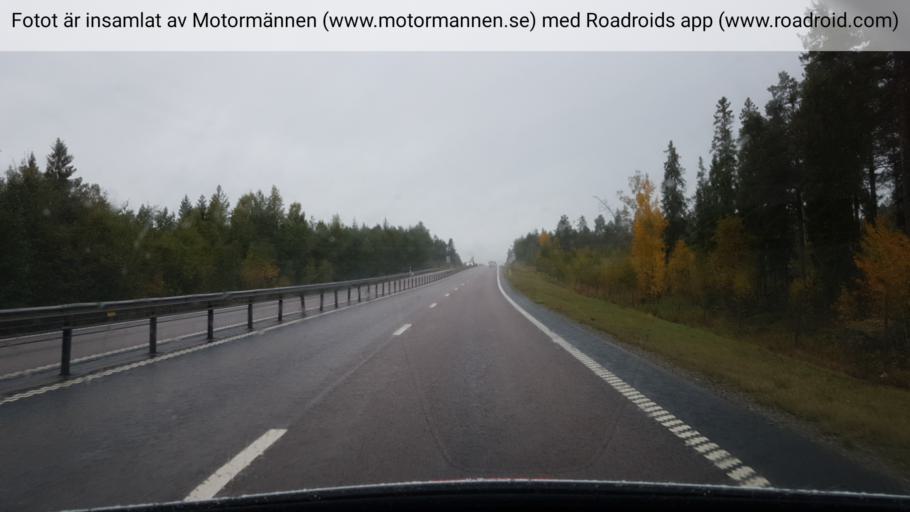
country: SE
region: Gaevleborg
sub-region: Hudiksvalls Kommun
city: Hudiksvall
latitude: 61.8568
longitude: 17.2056
